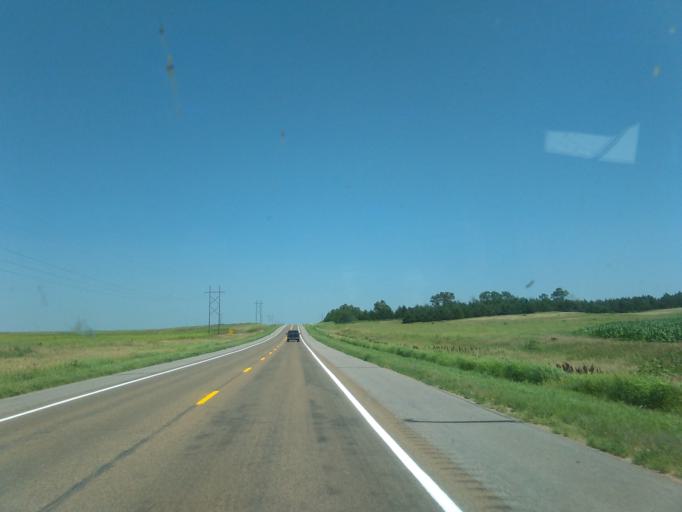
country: US
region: Nebraska
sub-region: Lincoln County
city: North Platte
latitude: 40.7905
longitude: -100.7537
